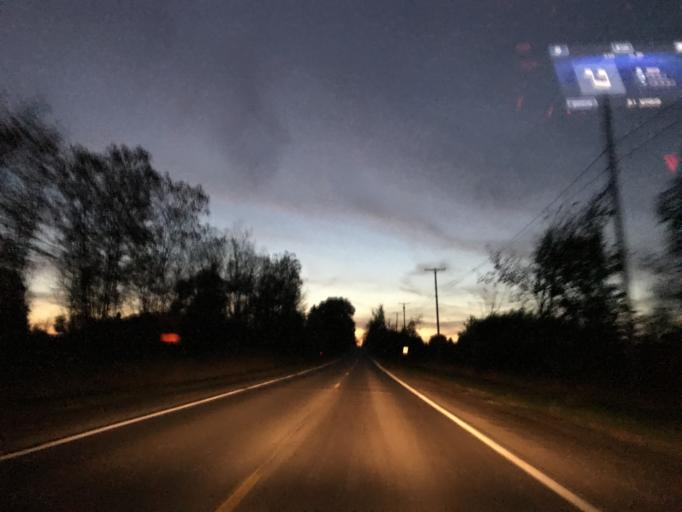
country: US
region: Michigan
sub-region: Oakland County
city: South Lyon
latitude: 42.4345
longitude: -83.5714
